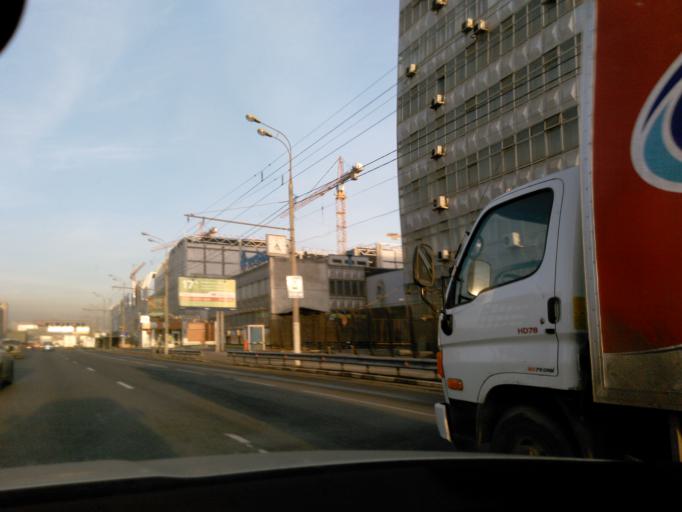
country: RU
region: Moskovskaya
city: Kozhukhovo
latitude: 55.7038
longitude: 37.6455
